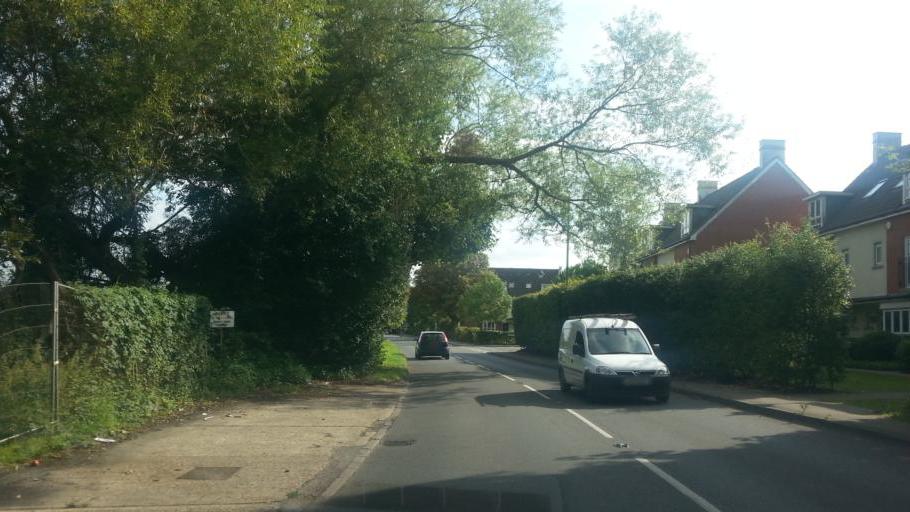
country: GB
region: England
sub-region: Surrey
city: Send
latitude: 51.3067
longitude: -0.5367
